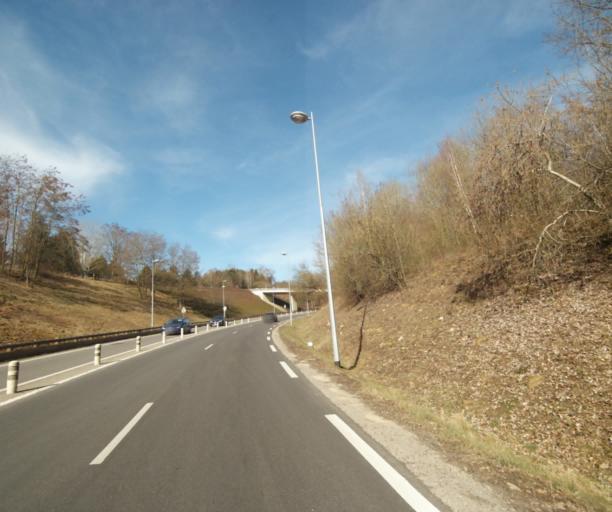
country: FR
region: Lorraine
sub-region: Departement de Meurthe-et-Moselle
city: Laxou
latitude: 48.6855
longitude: 6.1325
